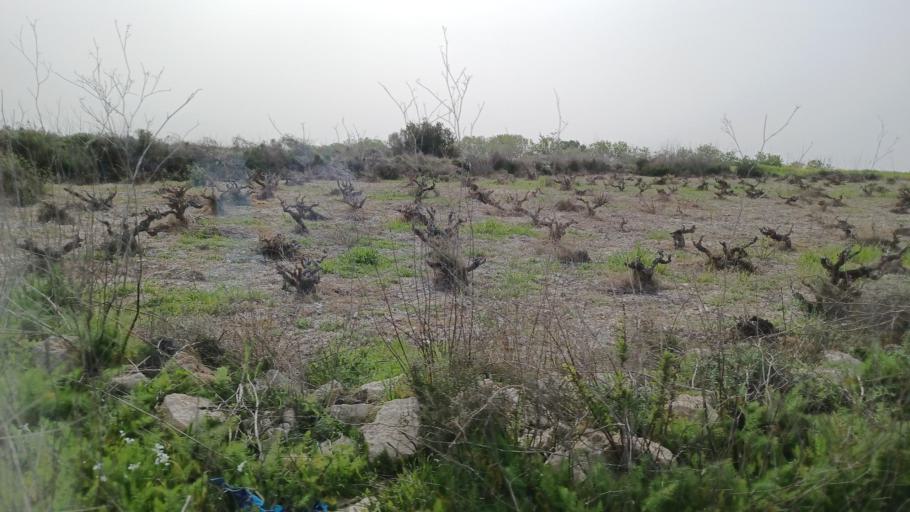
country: CY
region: Pafos
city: Pegeia
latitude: 34.9475
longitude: 32.3779
